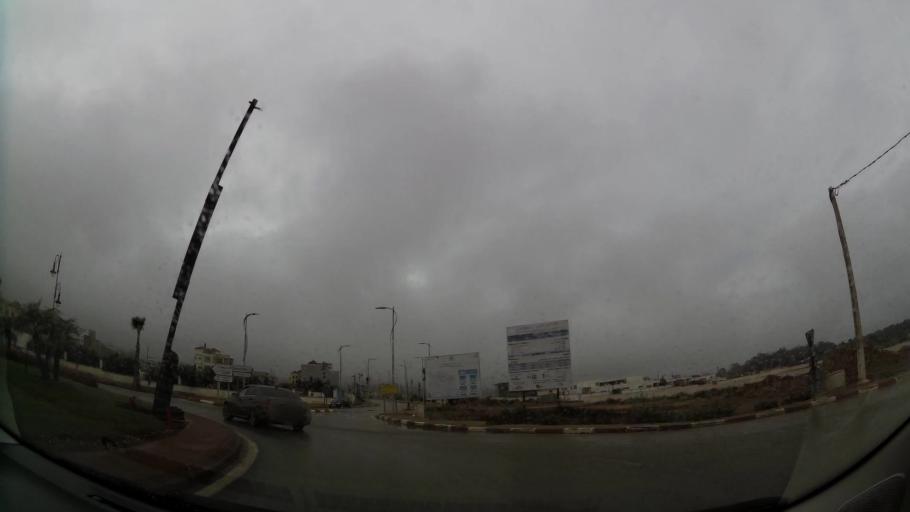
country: MA
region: Taza-Al Hoceima-Taounate
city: Imzourene
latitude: 35.1966
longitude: -3.8946
